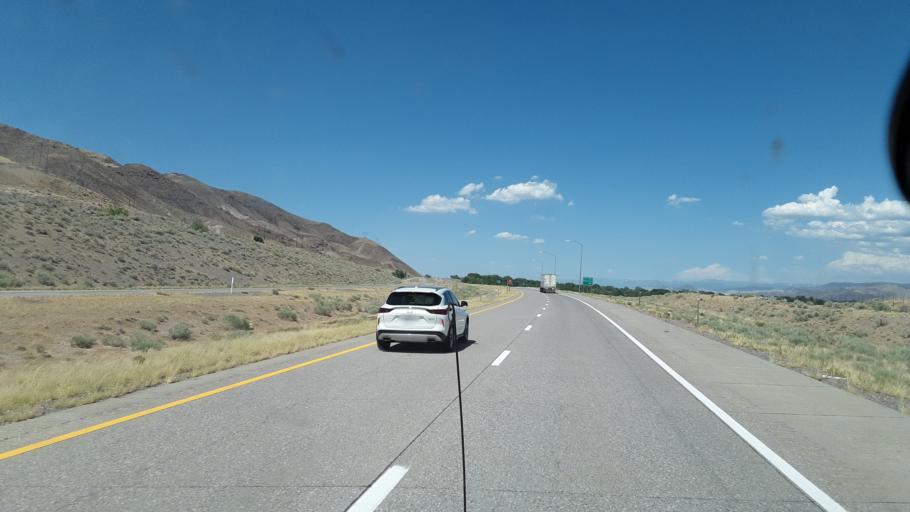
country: US
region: Utah
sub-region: Sevier County
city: Monroe
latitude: 38.6731
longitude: -112.1624
